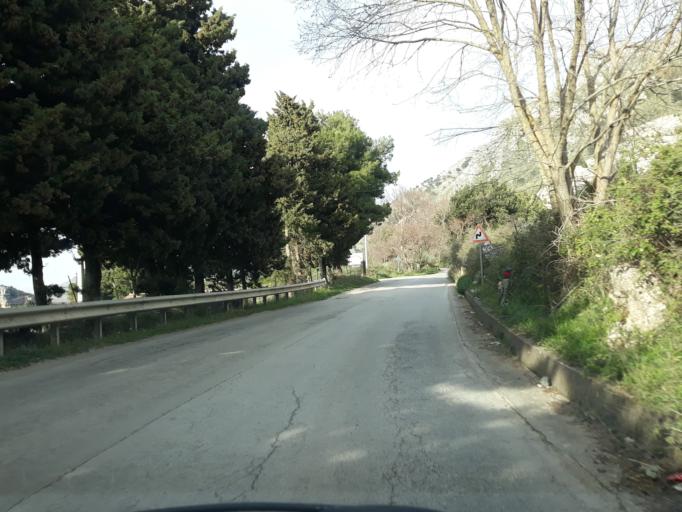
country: IT
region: Sicily
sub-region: Palermo
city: Torretta
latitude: 38.1064
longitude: 13.2341
